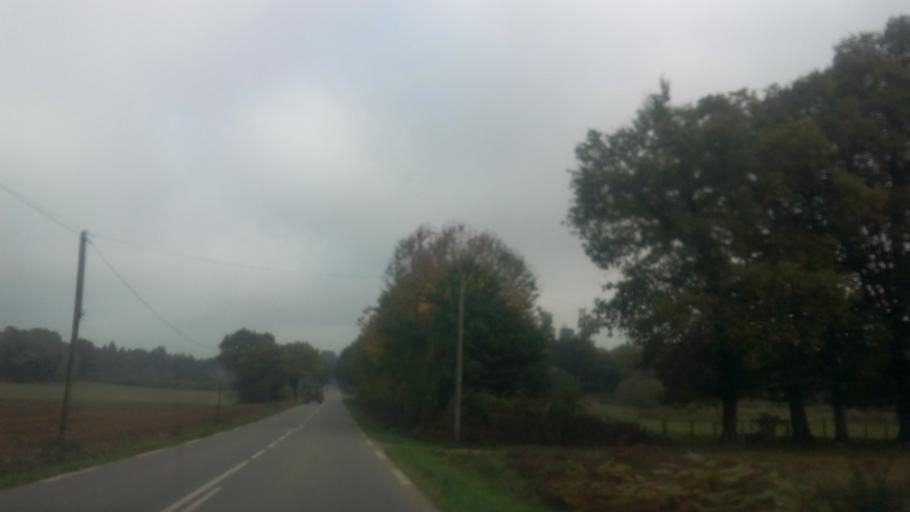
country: FR
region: Pays de la Loire
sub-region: Departement de la Loire-Atlantique
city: Avessac
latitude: 47.6362
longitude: -1.9263
